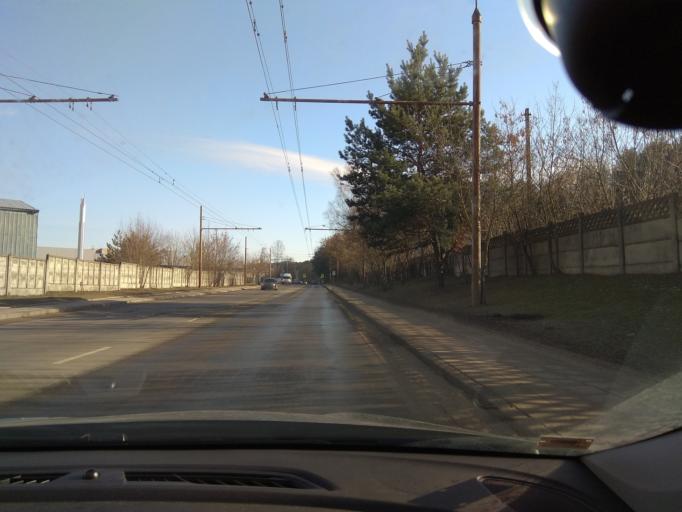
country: LT
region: Vilnius County
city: Lazdynai
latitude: 54.6462
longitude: 25.1924
